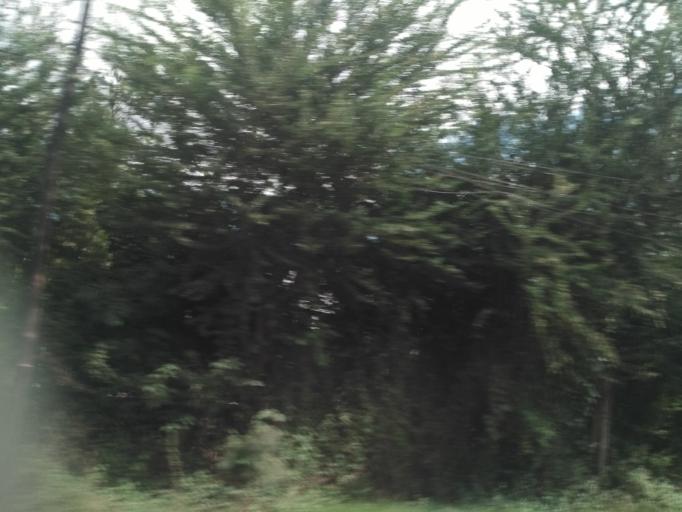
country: TZ
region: Mwanza
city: Mwanza
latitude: -2.5143
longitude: 32.9072
